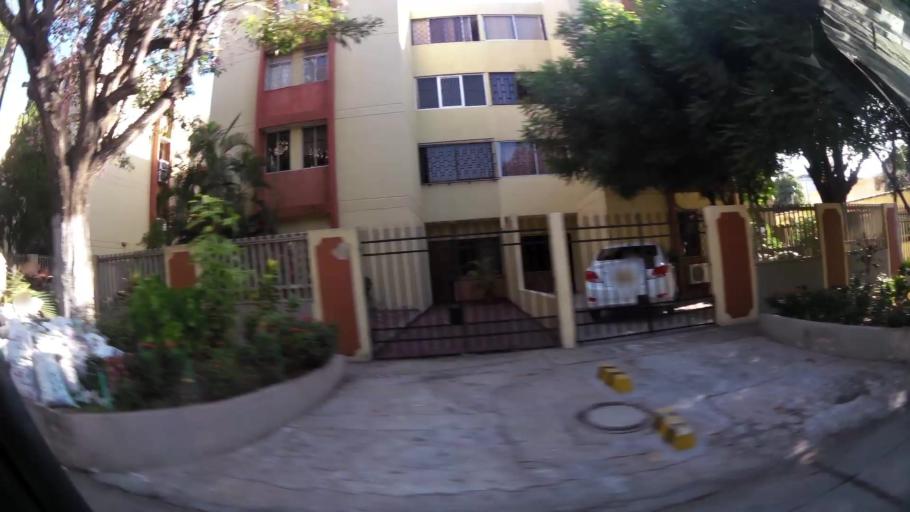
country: CO
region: Atlantico
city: Barranquilla
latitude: 11.0046
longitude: -74.7985
